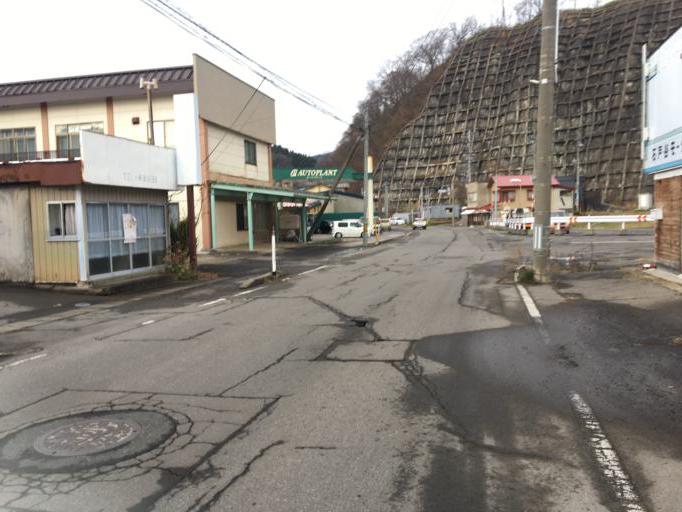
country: JP
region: Aomori
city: Hirosaki
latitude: 40.5229
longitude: 140.5644
